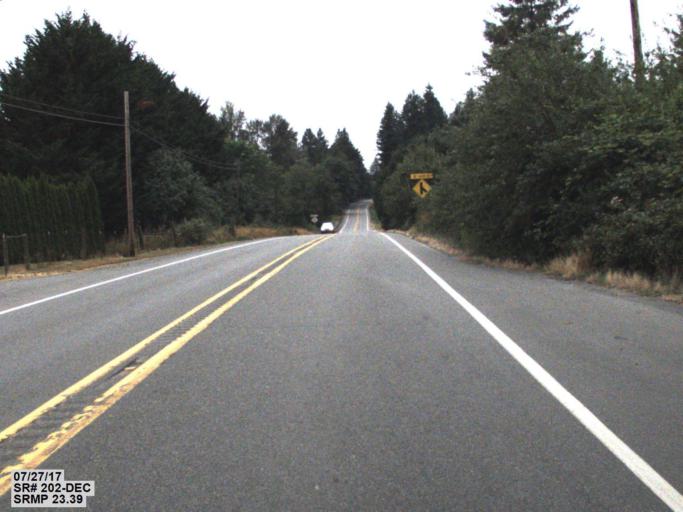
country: US
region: Washington
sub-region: King County
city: Fall City
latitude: 47.5605
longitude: -121.8582
